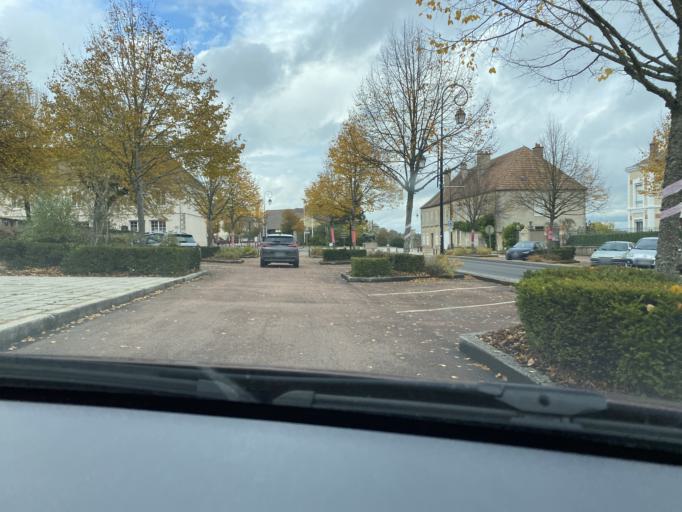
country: FR
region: Bourgogne
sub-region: Departement de la Cote-d'Or
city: Saulieu
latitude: 47.2806
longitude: 4.2312
